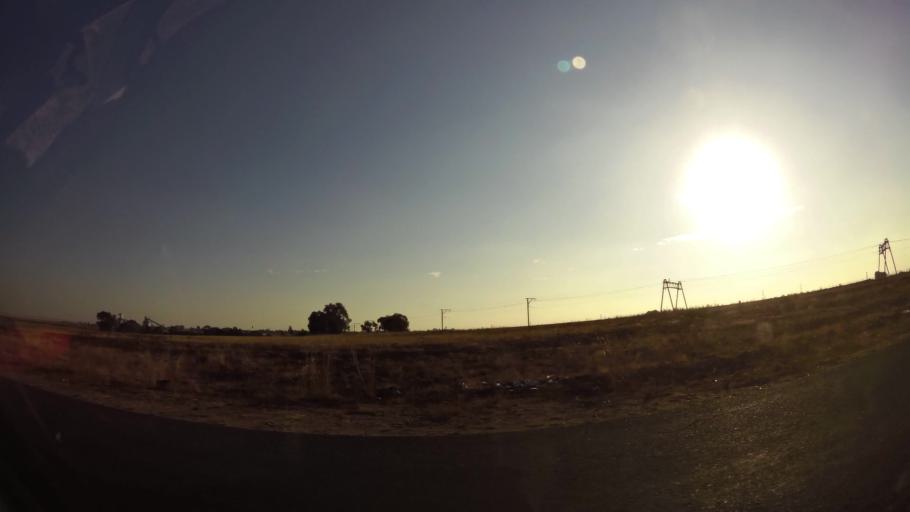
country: ZA
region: Gauteng
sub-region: West Rand District Municipality
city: Randfontein
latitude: -26.2007
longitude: 27.6749
